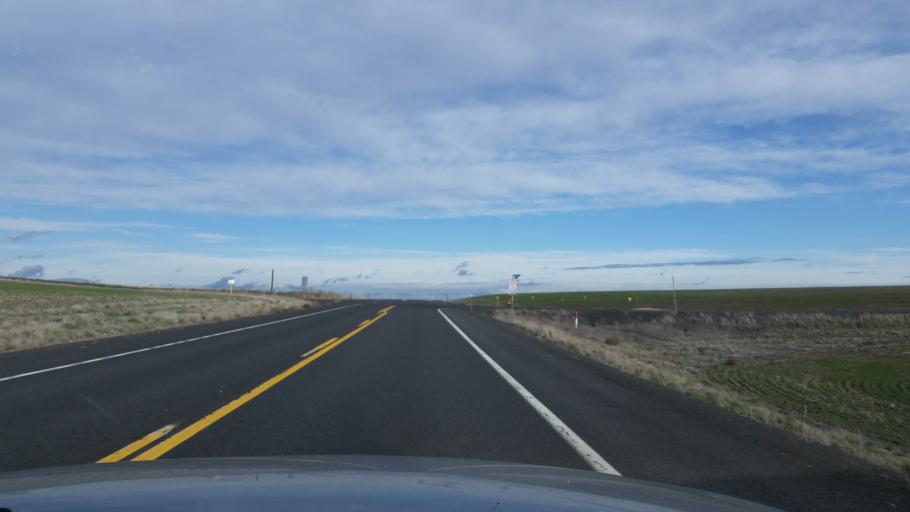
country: US
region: Washington
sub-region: Adams County
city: Ritzville
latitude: 47.3955
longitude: -118.4025
